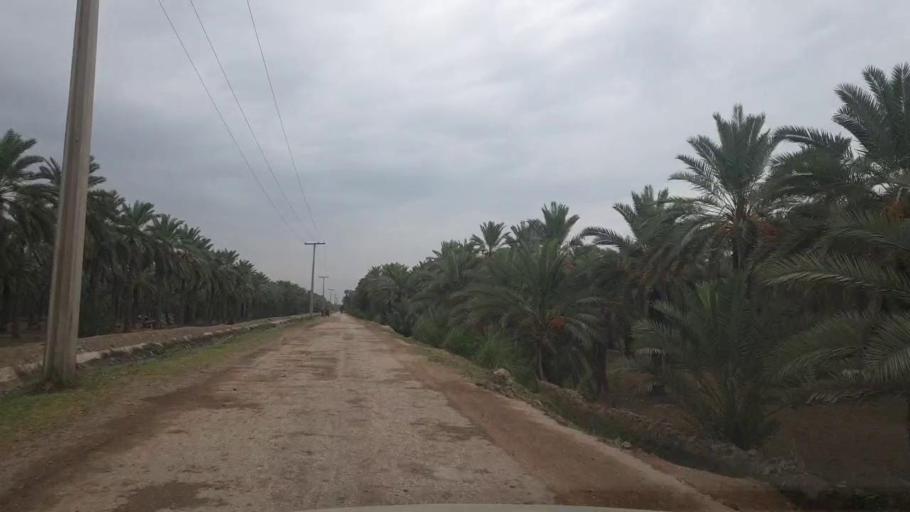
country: PK
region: Sindh
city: Khairpur
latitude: 27.6102
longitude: 68.8172
